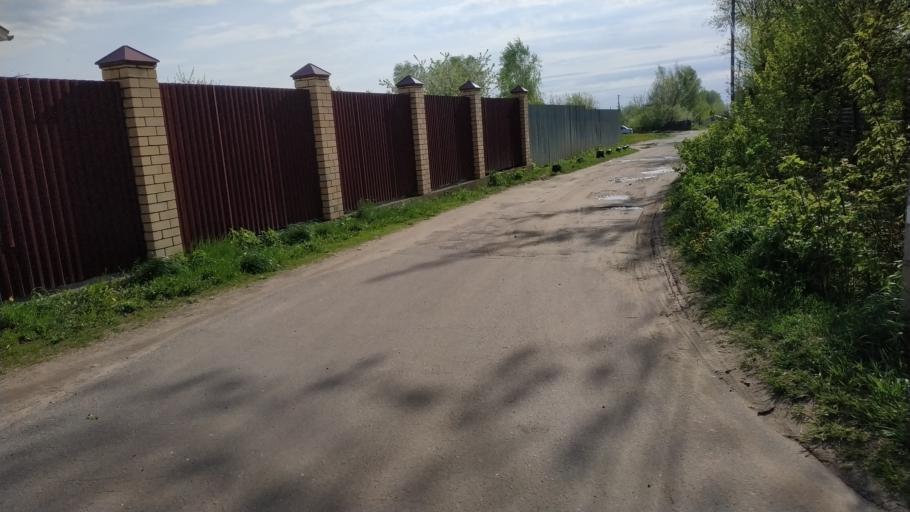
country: RU
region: Moskovskaya
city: Ramenskoye
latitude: 55.5472
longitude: 38.2436
